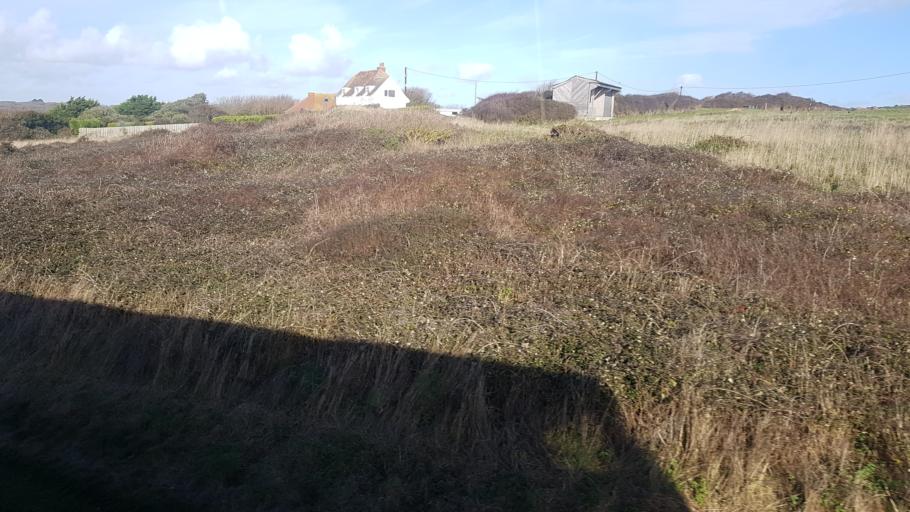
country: GB
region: England
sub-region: Isle of Wight
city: Freshwater
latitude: 50.6700
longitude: -1.5067
